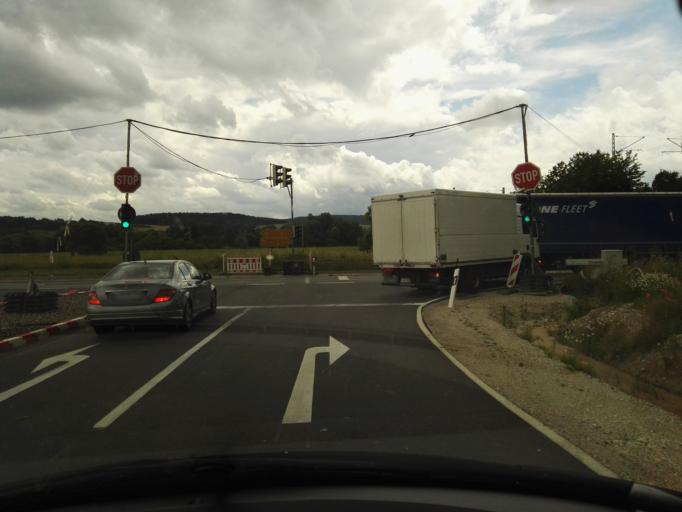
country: DE
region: Bavaria
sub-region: Upper Franconia
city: Redwitz an der Rodach
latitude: 50.1593
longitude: 11.1961
